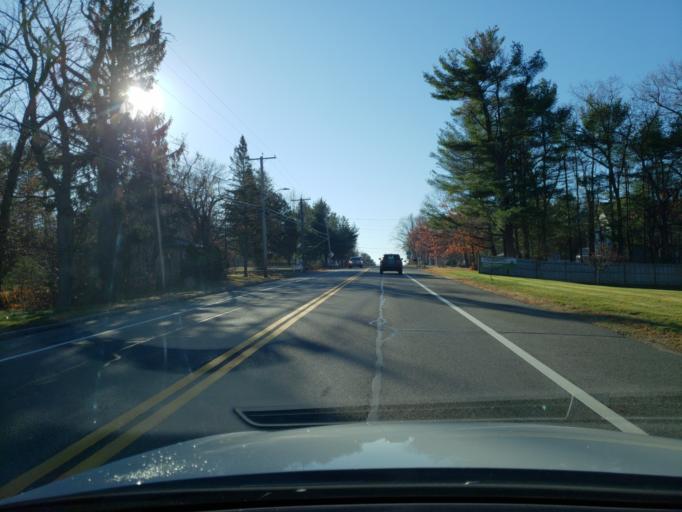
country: US
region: Massachusetts
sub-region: Essex County
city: Andover
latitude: 42.6094
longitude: -71.1231
